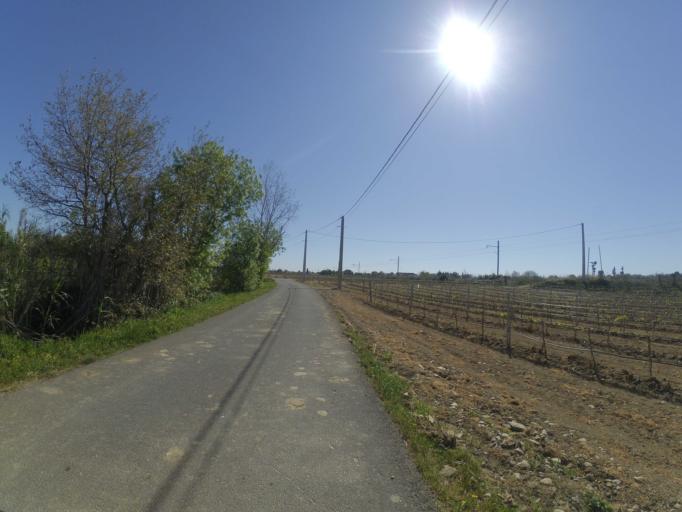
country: FR
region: Languedoc-Roussillon
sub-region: Departement des Pyrenees-Orientales
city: Millas
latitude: 42.6843
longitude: 2.7108
